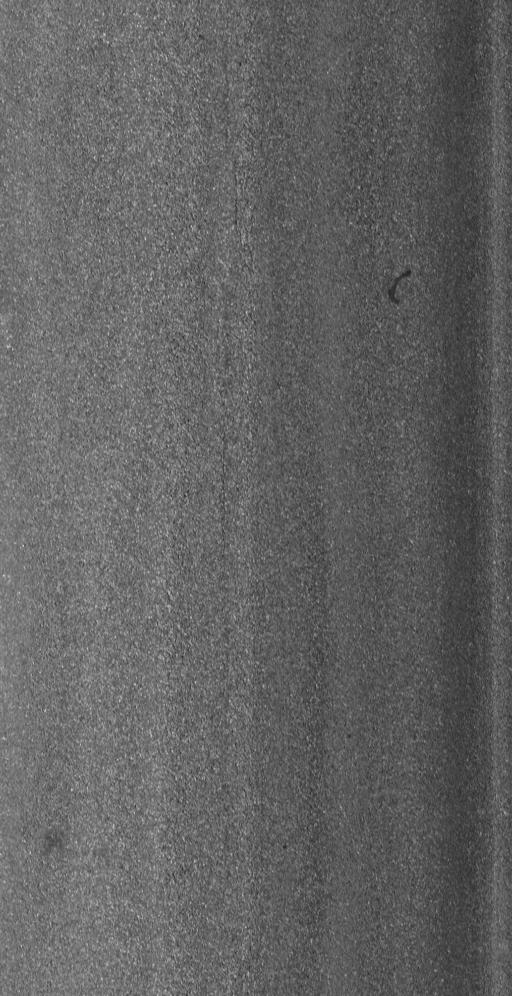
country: US
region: New Hampshire
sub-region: Grafton County
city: Lyme
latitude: 43.8130
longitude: -72.2145
